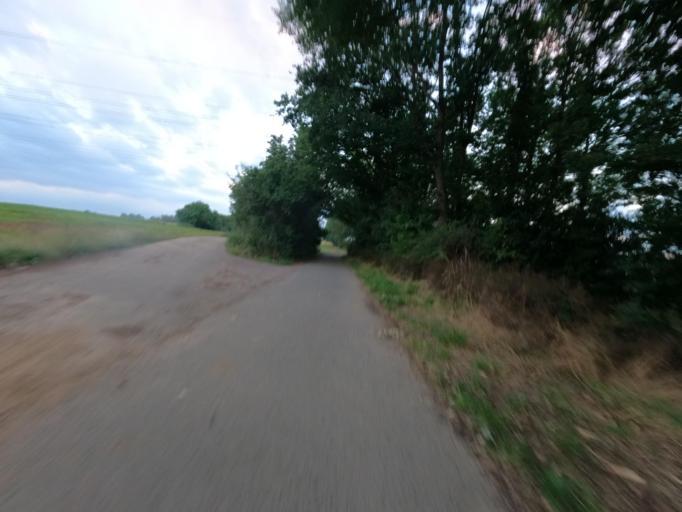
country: DE
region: North Rhine-Westphalia
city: Baesweiler
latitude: 50.9518
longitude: 6.1909
